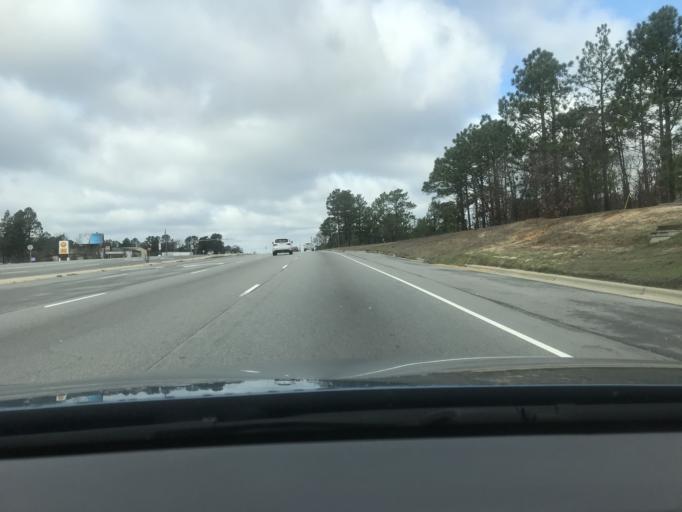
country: US
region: North Carolina
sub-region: Cumberland County
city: Spring Lake
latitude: 35.2580
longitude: -79.0396
